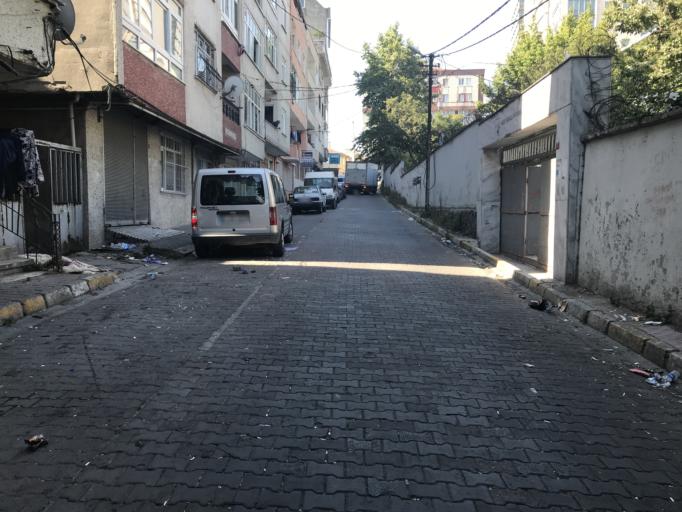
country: TR
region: Istanbul
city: Esenler
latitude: 41.0598
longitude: 28.9091
